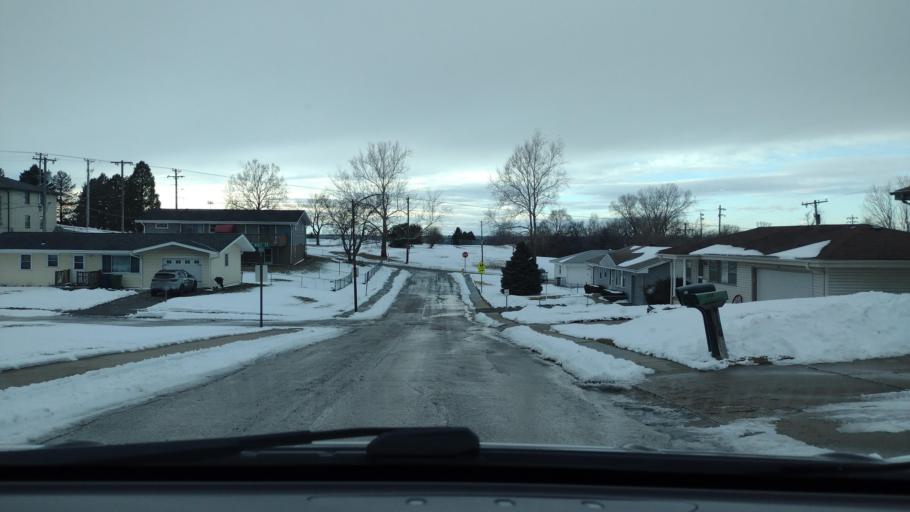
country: US
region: Nebraska
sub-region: Sarpy County
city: La Vista
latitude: 41.1796
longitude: -95.9757
